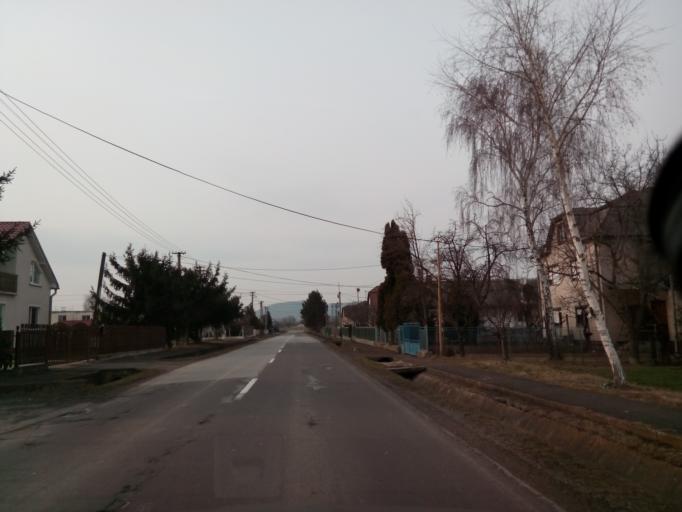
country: SK
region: Kosicky
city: Secovce
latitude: 48.6158
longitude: 21.6009
